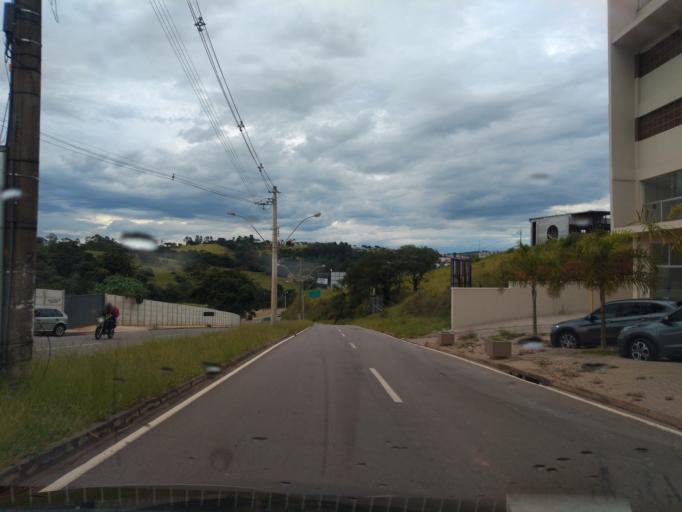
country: BR
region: Minas Gerais
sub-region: Varginha
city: Varginha
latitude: -21.5694
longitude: -45.4498
